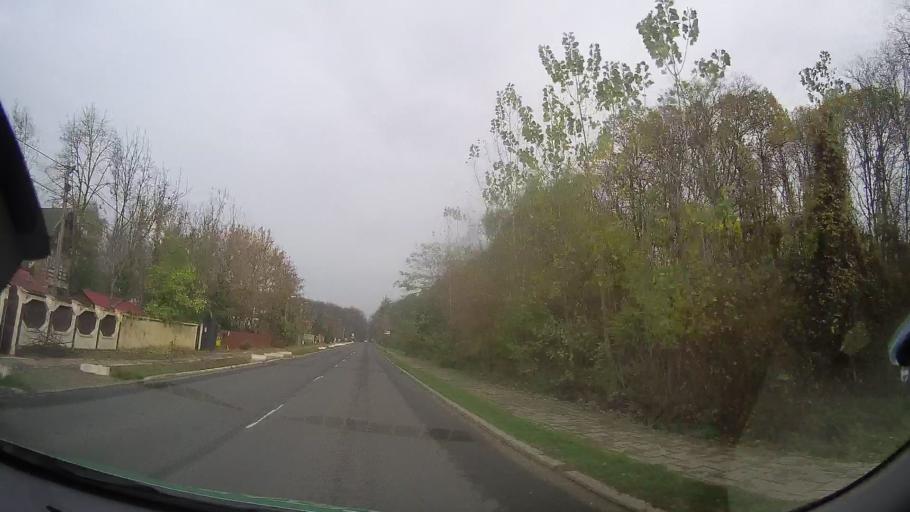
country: RO
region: Ilfov
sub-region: Comuna Snagov
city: Snagov
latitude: 44.7124
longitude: 26.1896
